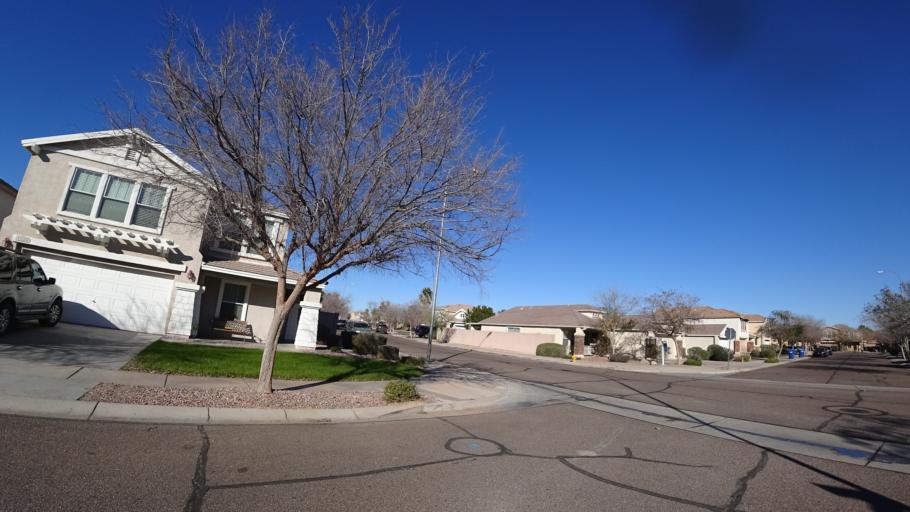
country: US
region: Arizona
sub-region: Maricopa County
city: Avondale
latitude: 33.4321
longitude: -112.3168
